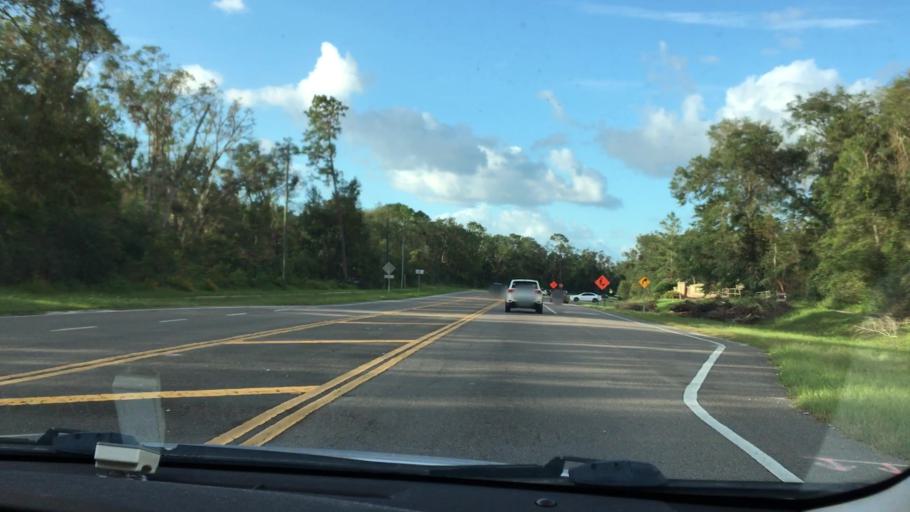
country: US
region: Florida
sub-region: Volusia County
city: Orange City
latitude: 28.9348
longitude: -81.2818
